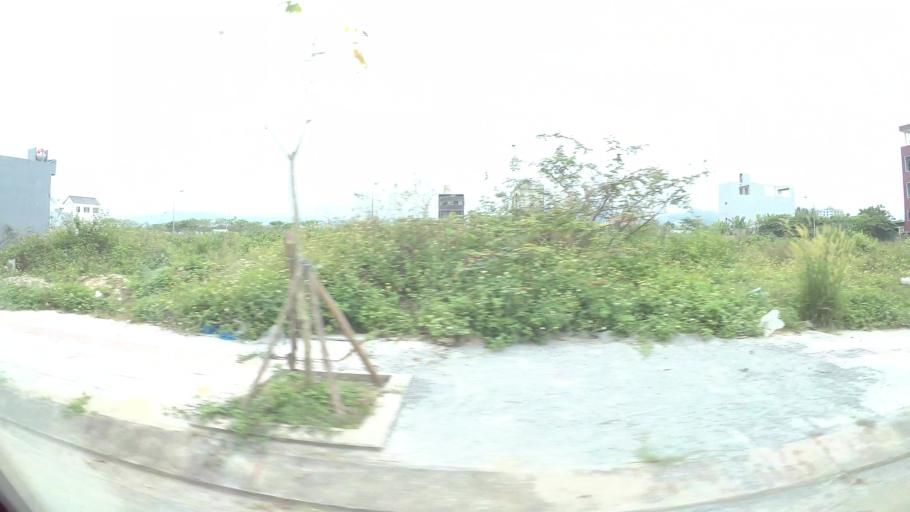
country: VN
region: Da Nang
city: Lien Chieu
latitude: 16.0758
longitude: 108.1601
